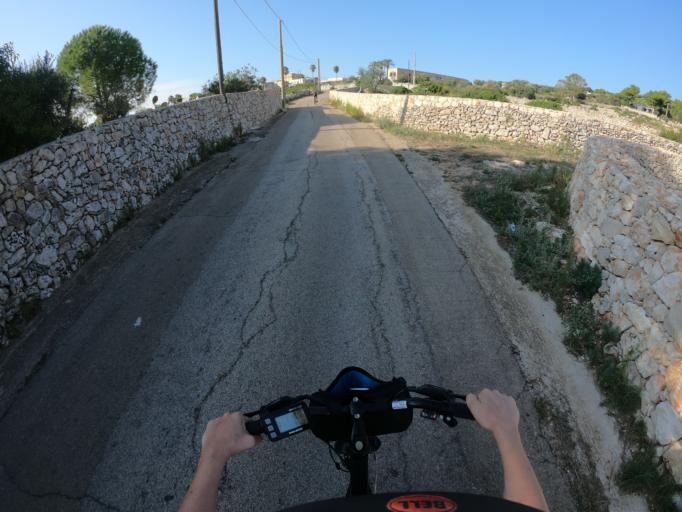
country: IT
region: Apulia
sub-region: Provincia di Lecce
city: Leuca
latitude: 39.8021
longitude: 18.3634
